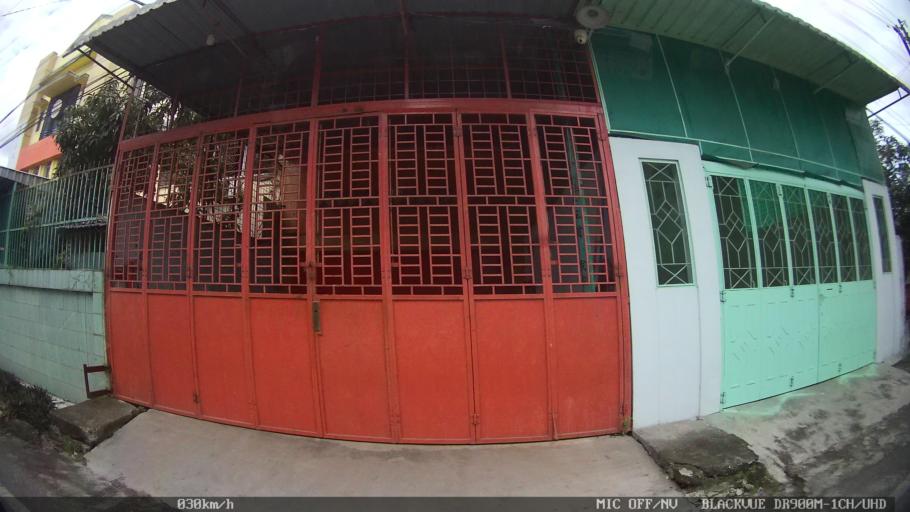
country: ID
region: North Sumatra
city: Percut
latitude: 3.5619
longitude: 98.8732
